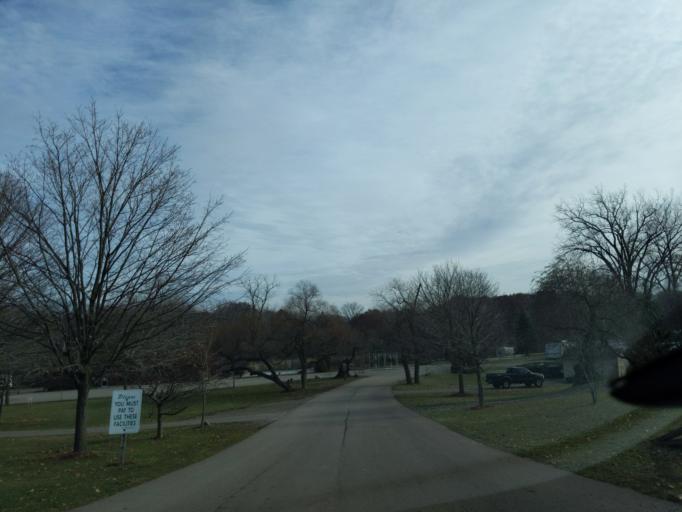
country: US
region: Michigan
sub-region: Ingham County
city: Holt
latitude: 42.6787
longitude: -84.5234
